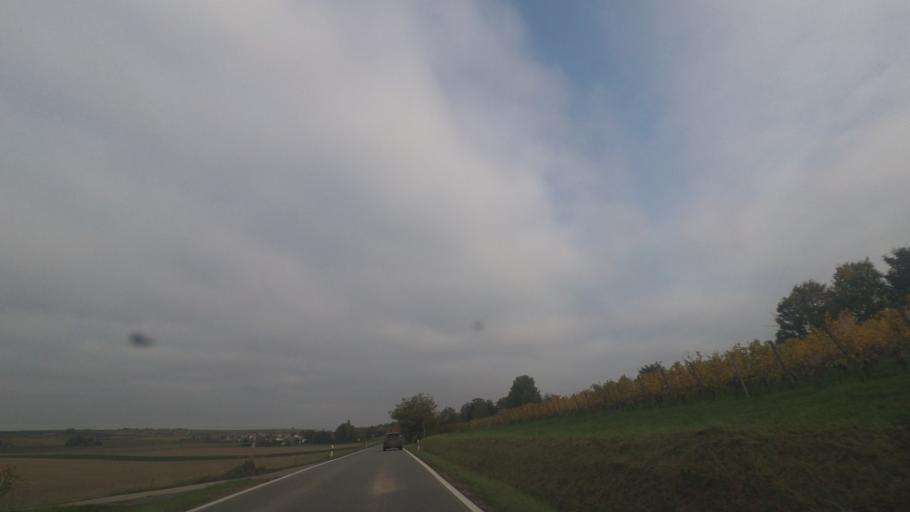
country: DE
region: Rheinland-Pfalz
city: Bechtheim
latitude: 49.7236
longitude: 8.2758
